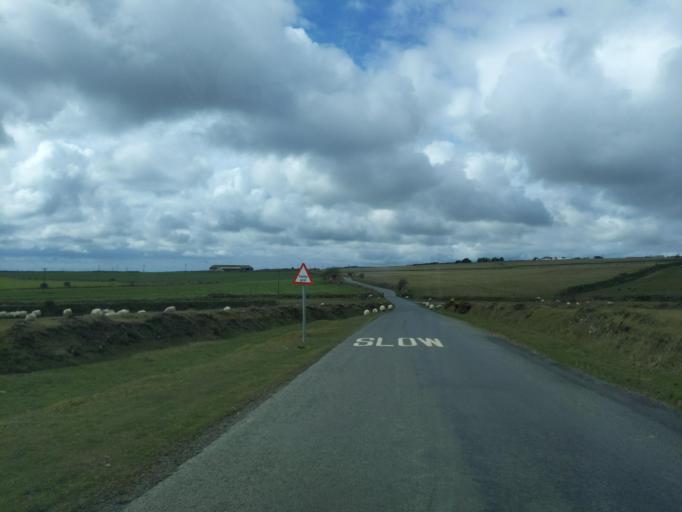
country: GB
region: England
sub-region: Cornwall
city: Camelford
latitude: 50.6400
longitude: -4.6316
